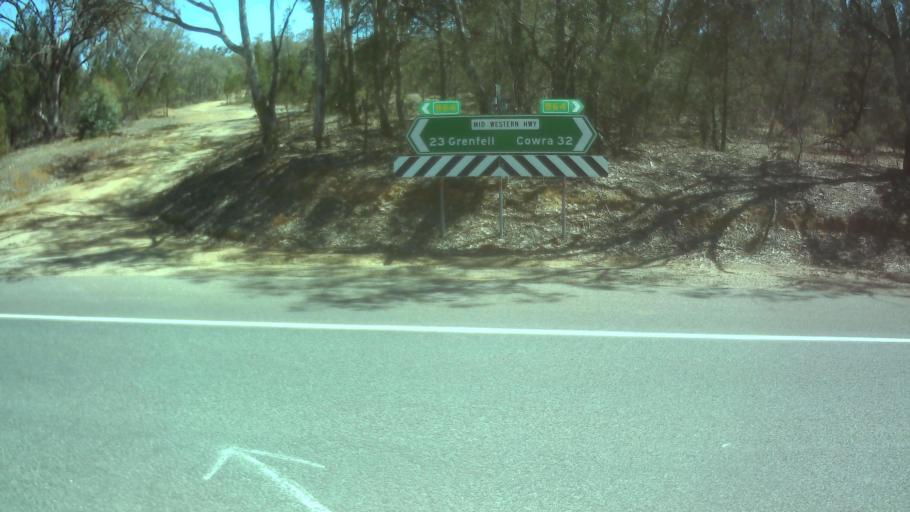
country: AU
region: New South Wales
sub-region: Weddin
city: Grenfell
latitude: -33.9388
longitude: 148.3848
